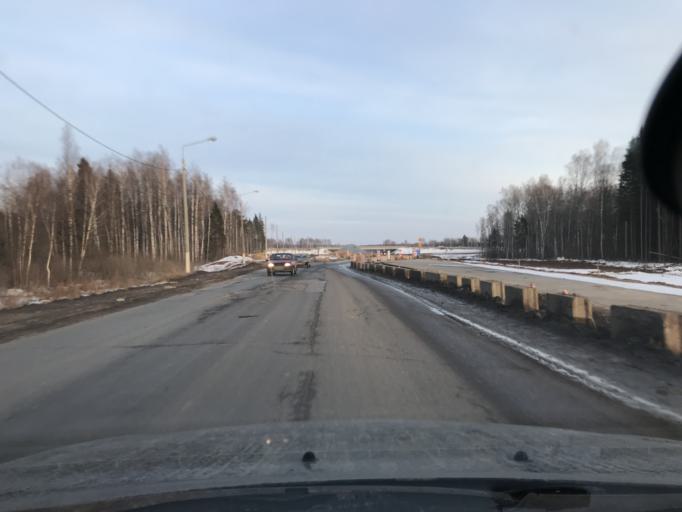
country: RU
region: Kaluga
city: Kaluga
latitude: 54.4625
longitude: 36.2646
